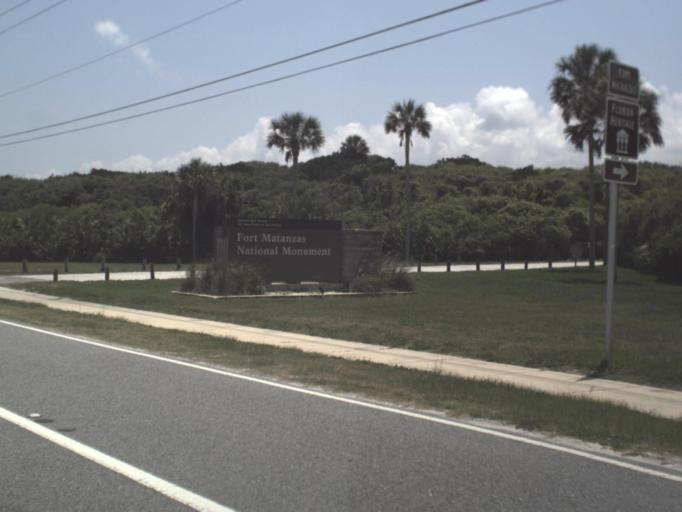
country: US
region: Florida
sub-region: Saint Johns County
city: Butler Beach
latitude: 29.7172
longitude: -81.2331
